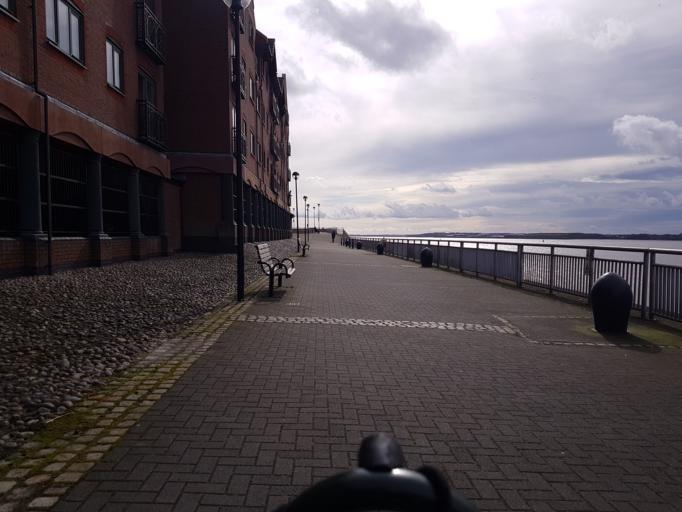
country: GB
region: England
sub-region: Liverpool
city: Liverpool
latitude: 53.3877
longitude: -2.9857
